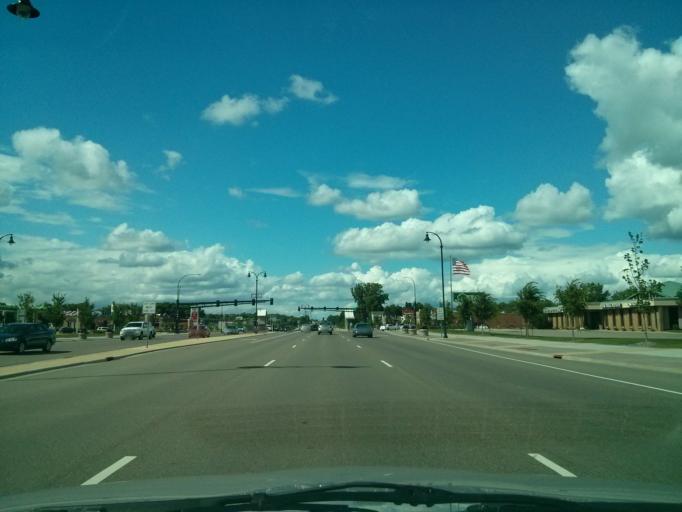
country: US
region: Minnesota
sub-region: Dakota County
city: Apple Valley
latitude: 44.7338
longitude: -93.2176
